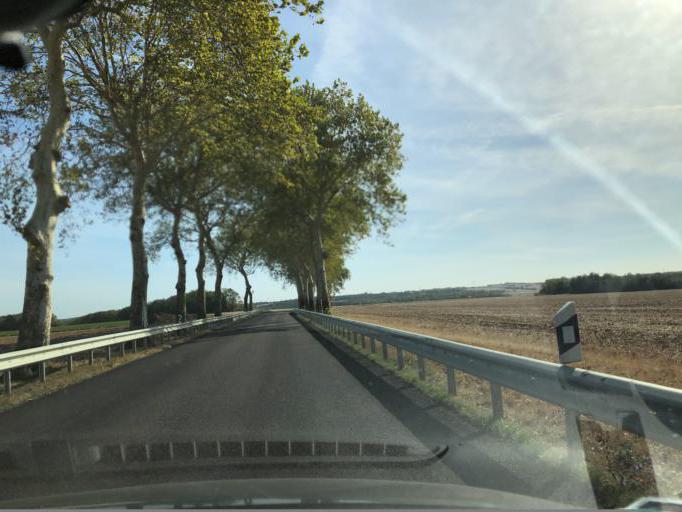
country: FR
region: Centre
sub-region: Departement du Loiret
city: Sermaises
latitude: 48.3532
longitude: 2.2776
